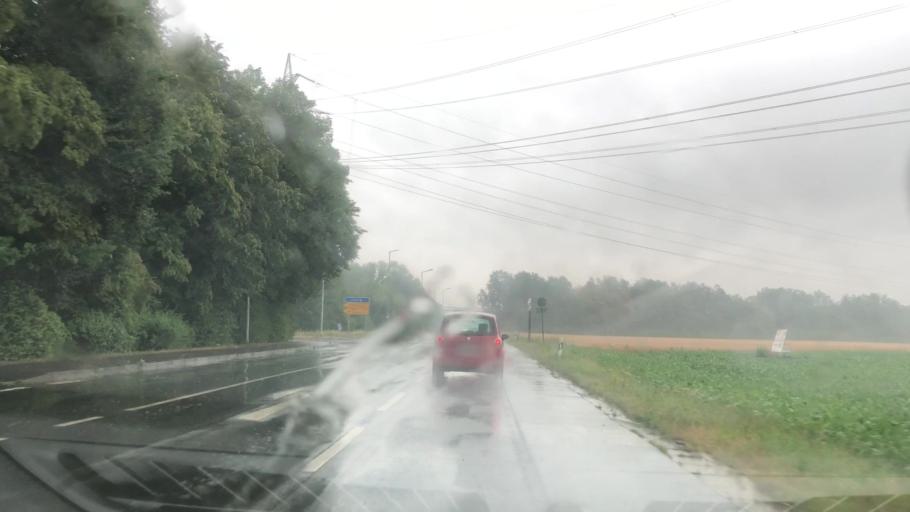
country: DE
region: North Rhine-Westphalia
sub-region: Regierungsbezirk Detmold
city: Minden
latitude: 52.2771
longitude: 8.9631
